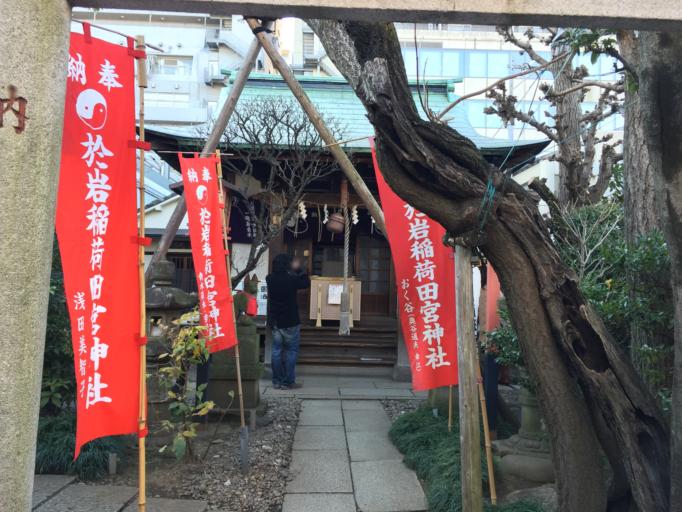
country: JP
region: Tokyo
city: Tokyo
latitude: 35.6855
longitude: 139.7210
